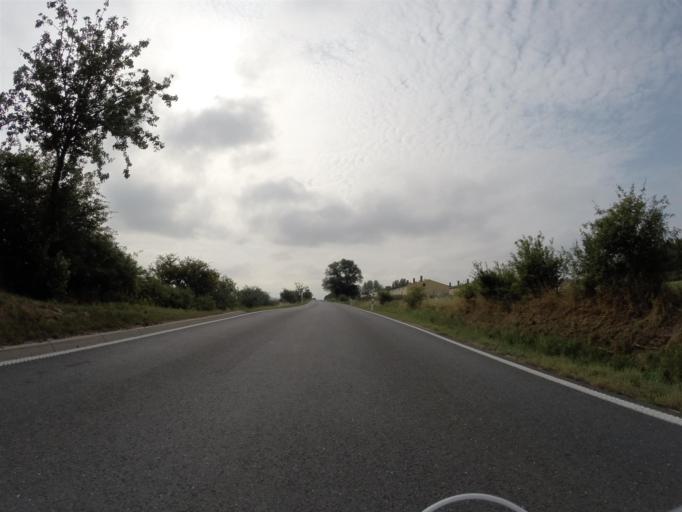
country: DE
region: Thuringia
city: Schongleina
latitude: 50.9254
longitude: 11.7265
